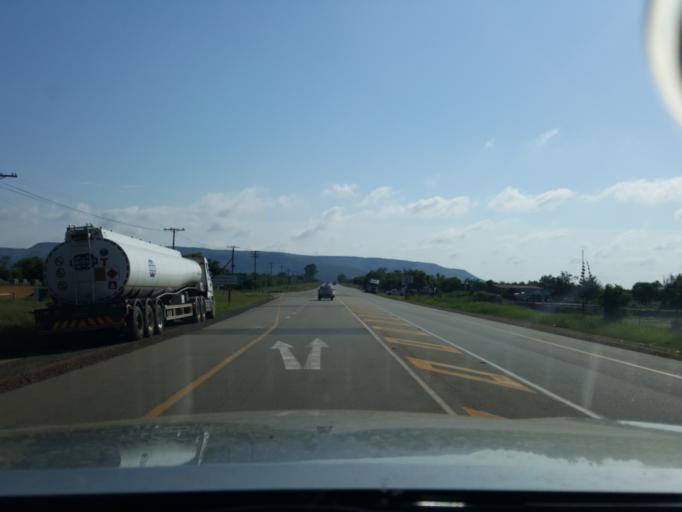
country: ZA
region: North-West
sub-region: Ngaka Modiri Molema District Municipality
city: Zeerust
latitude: -25.5615
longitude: 26.0613
